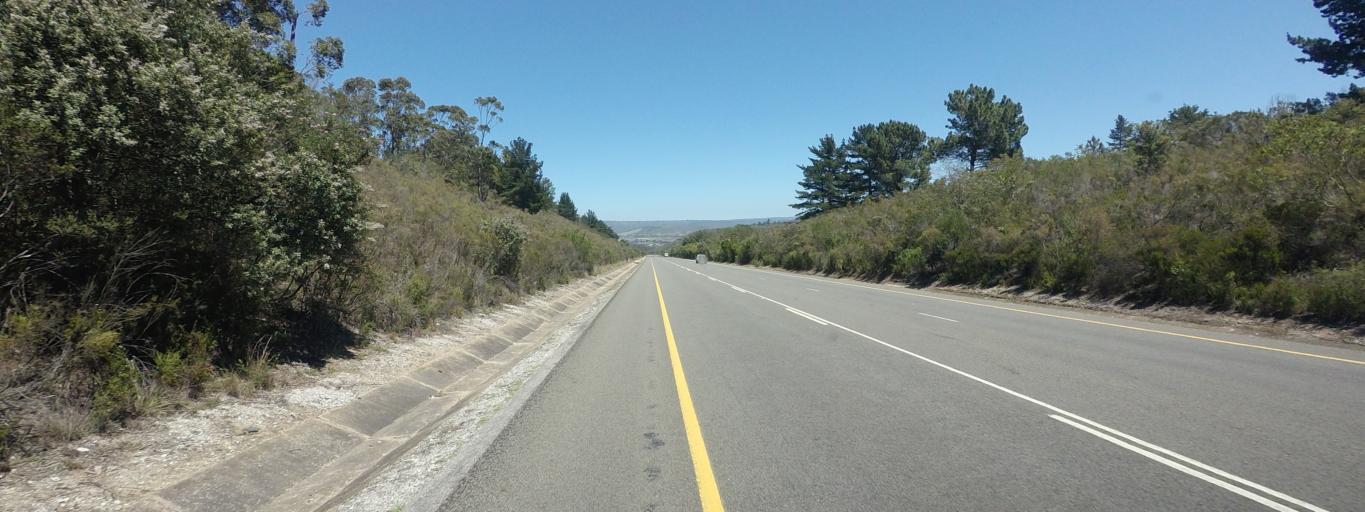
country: ZA
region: Western Cape
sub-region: Eden District Municipality
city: Plettenberg Bay
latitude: -34.0006
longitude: 23.4304
